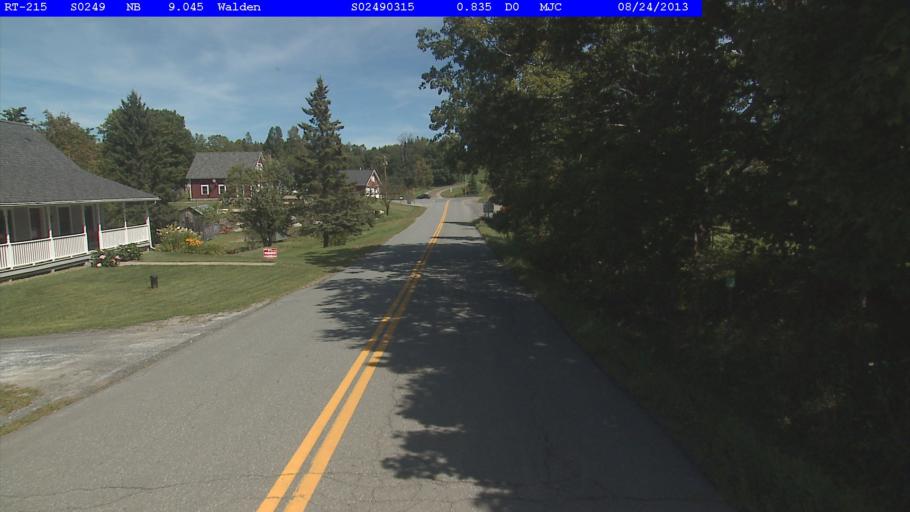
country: US
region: Vermont
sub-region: Caledonia County
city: Hardwick
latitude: 44.4510
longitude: -72.2576
